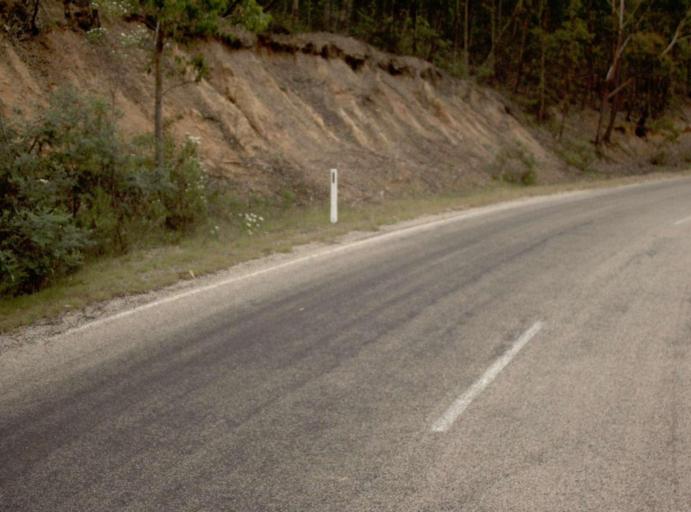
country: AU
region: Victoria
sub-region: East Gippsland
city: Bairnsdale
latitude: -37.6038
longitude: 147.1932
